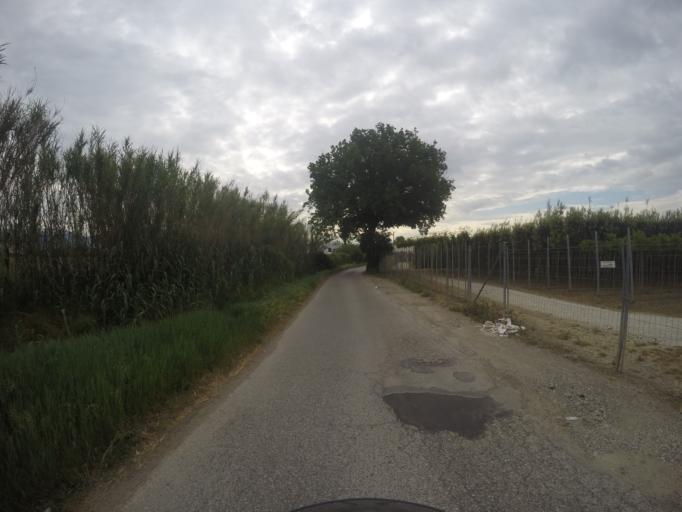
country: IT
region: Tuscany
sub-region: Provincia di Prato
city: Fornacelle
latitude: 43.8939
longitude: 11.0521
